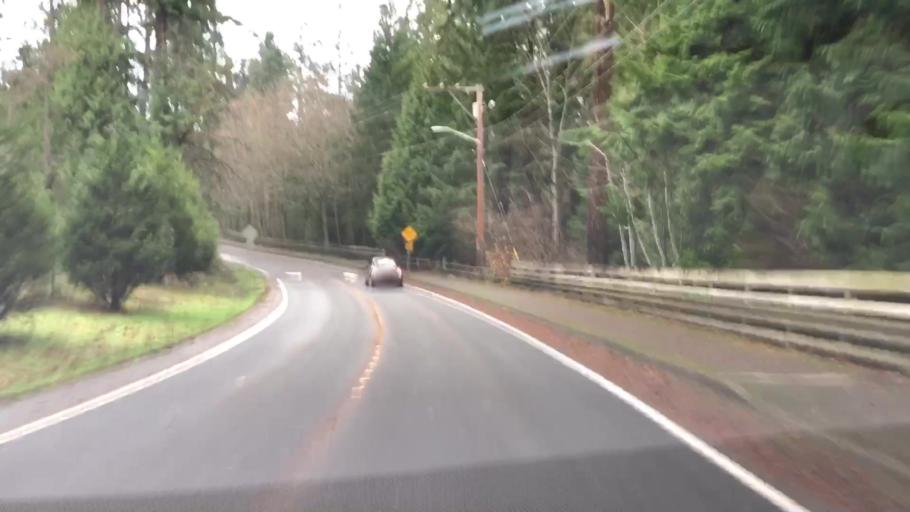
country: US
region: Washington
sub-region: King County
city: West Lake Sammamish
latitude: 47.5898
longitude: -122.1160
